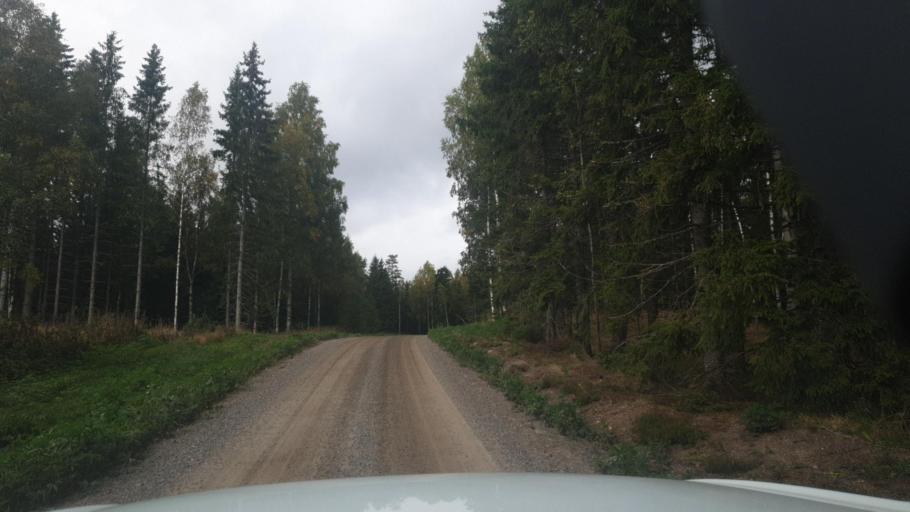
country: SE
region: Vaermland
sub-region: Torsby Kommun
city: Torsby
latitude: 59.9417
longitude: 12.8042
